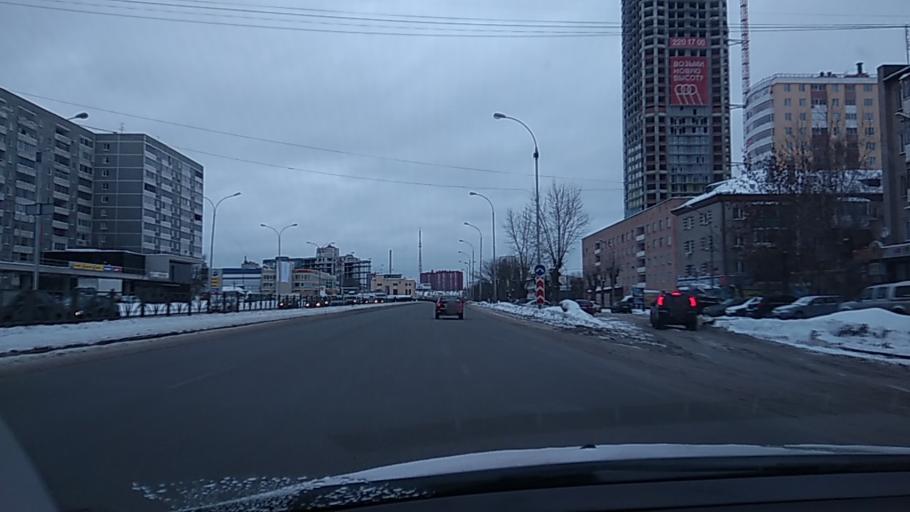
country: RU
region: Sverdlovsk
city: Yekaterinburg
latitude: 56.8110
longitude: 60.6298
